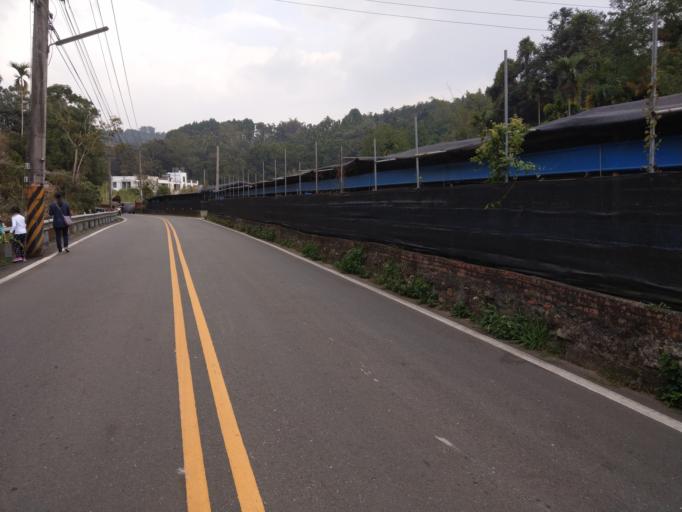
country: TW
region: Taiwan
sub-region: Nantou
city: Puli
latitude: 23.9040
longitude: 120.9151
